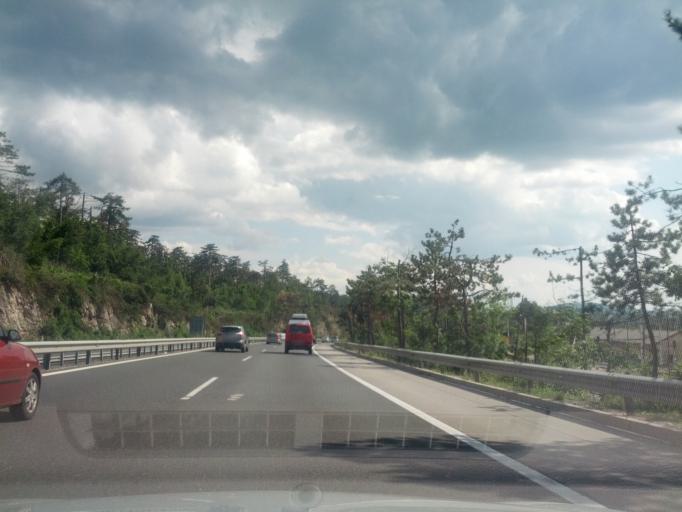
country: SI
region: Postojna
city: Postojna
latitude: 45.7737
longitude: 14.2223
